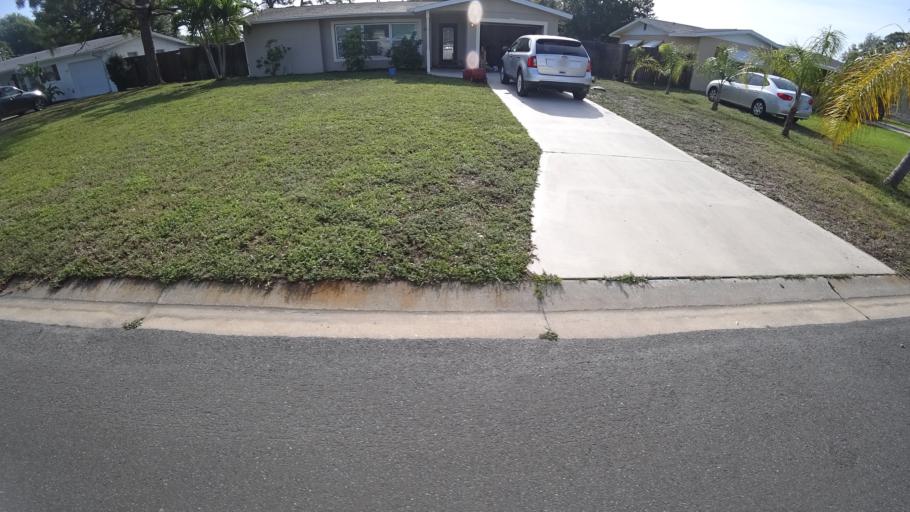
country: US
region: Florida
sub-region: Manatee County
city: West Bradenton
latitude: 27.5014
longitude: -82.6234
